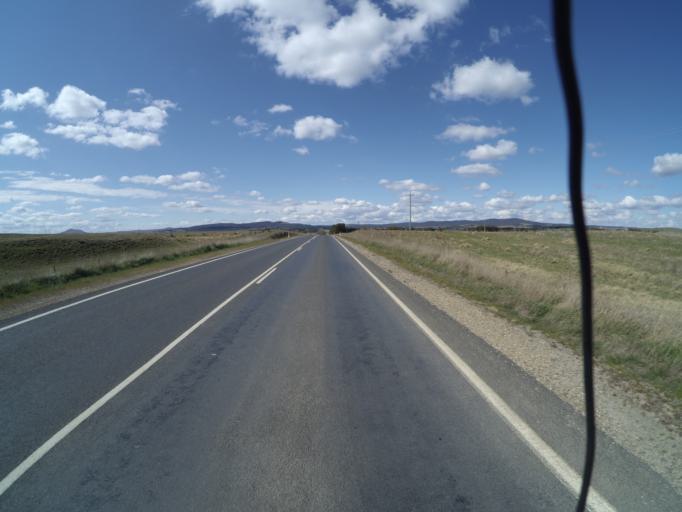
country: AU
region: New South Wales
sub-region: Palerang
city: Bungendore
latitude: -35.2156
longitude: 149.4671
